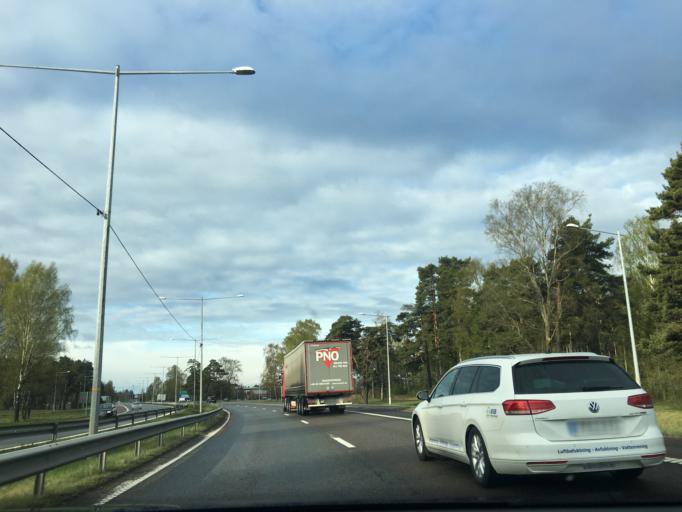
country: SE
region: Vaermland
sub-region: Karlstads Kommun
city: Karlstad
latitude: 59.3961
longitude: 13.4982
